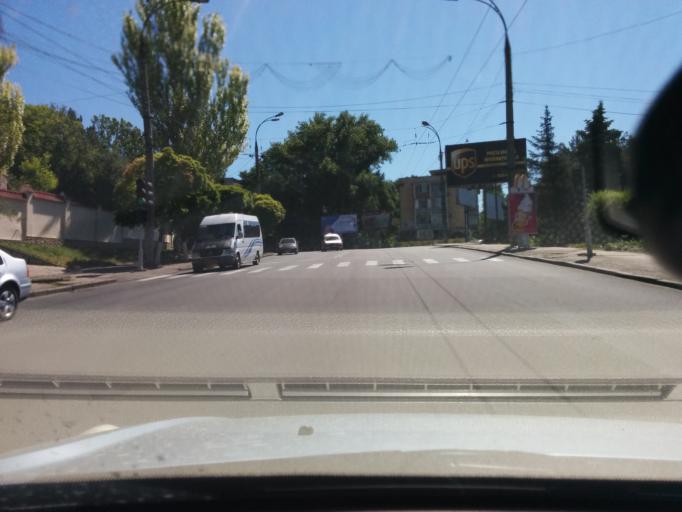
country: MD
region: Chisinau
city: Chisinau
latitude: 47.0390
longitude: 28.8580
